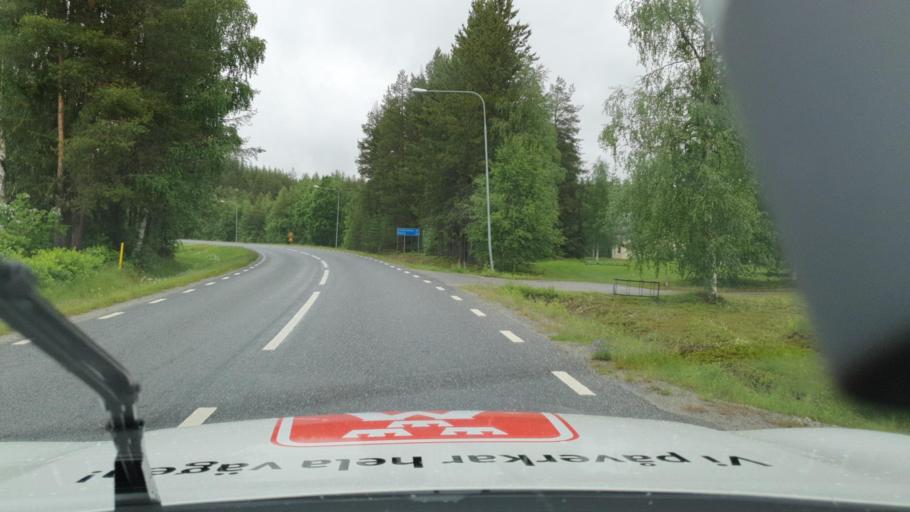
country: SE
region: Vaesterbotten
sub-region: Asele Kommun
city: Asele
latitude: 63.9415
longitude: 17.2829
